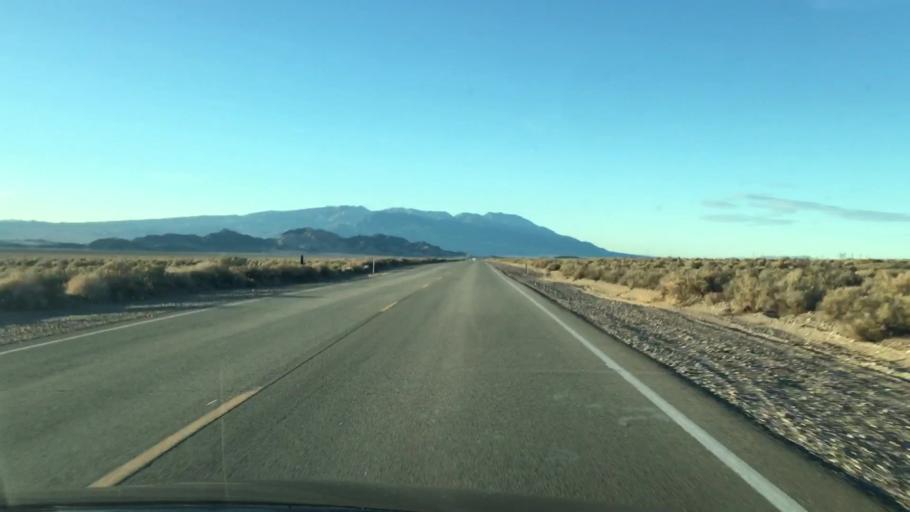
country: US
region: California
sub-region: San Bernardino County
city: Fort Irwin
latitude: 35.3505
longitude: -116.0904
